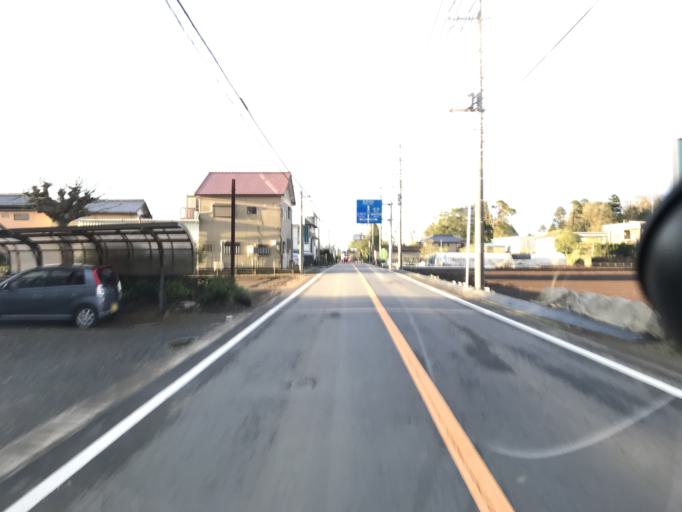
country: JP
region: Chiba
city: Sawara
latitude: 35.7981
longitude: 140.4550
